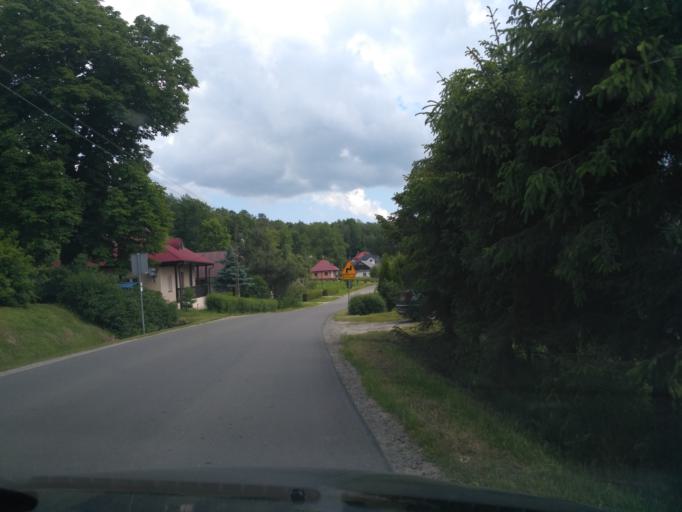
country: PL
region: Subcarpathian Voivodeship
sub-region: Powiat rzeszowski
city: Blazowa
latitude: 49.8744
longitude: 22.0673
